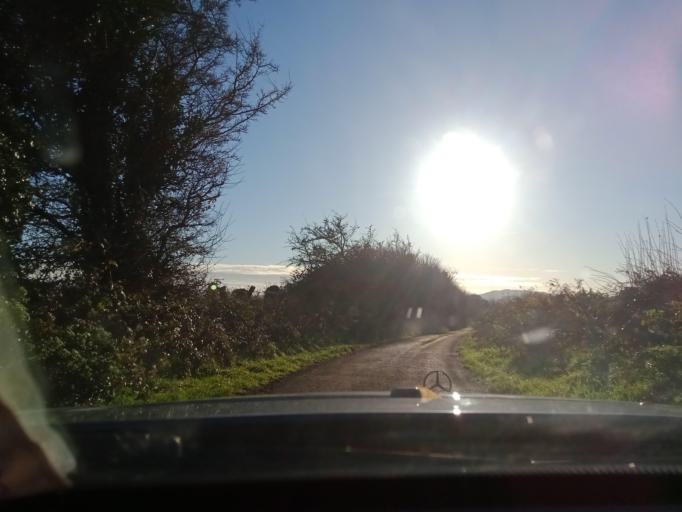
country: IE
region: Leinster
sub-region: Kilkenny
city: Callan
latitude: 52.4545
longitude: -7.4210
